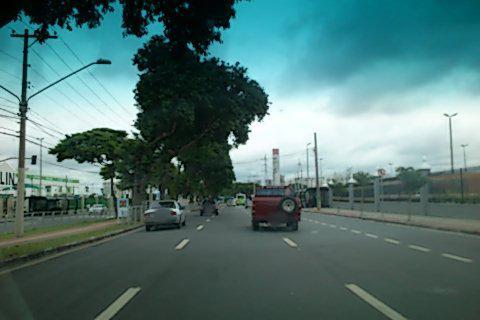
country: BR
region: Sao Paulo
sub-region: Sao Jose Dos Campos
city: Sao Jose dos Campos
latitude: -23.2177
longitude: -45.8939
